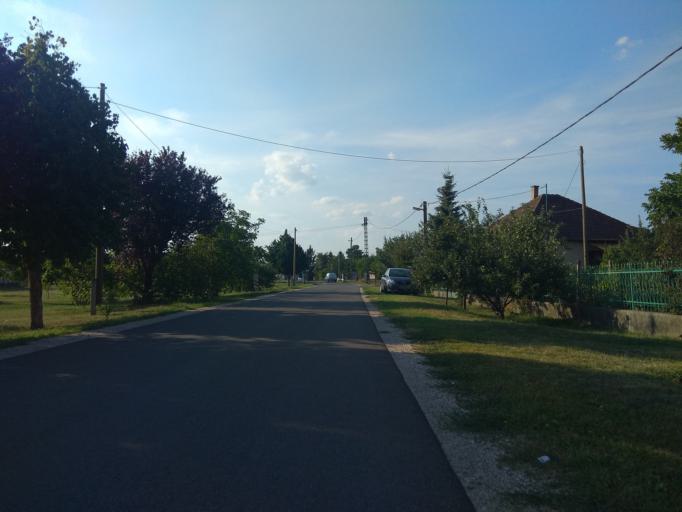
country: HU
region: Borsod-Abauj-Zemplen
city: Emod
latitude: 47.8896
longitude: 20.7645
